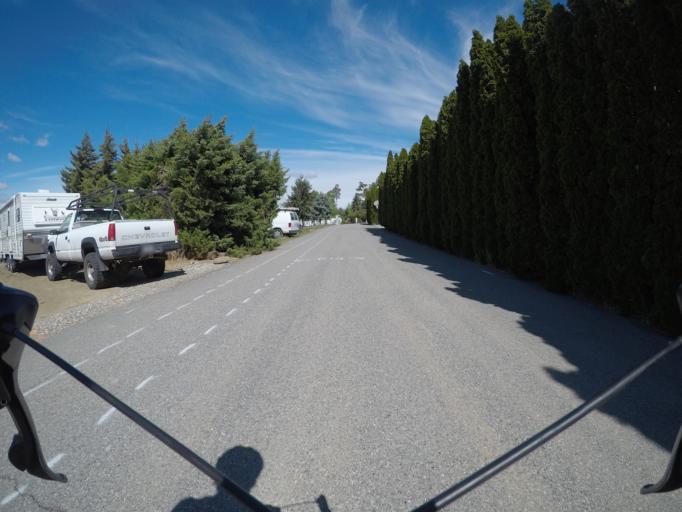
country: US
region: Washington
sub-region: Chelan County
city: South Wenatchee
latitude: 47.4013
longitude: -120.2765
